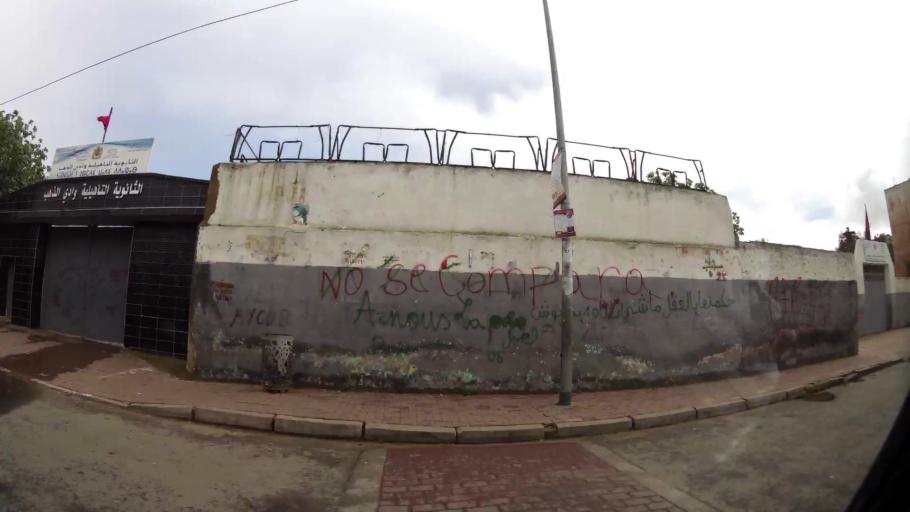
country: MA
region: Grand Casablanca
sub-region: Casablanca
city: Casablanca
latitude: 33.5405
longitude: -7.5731
